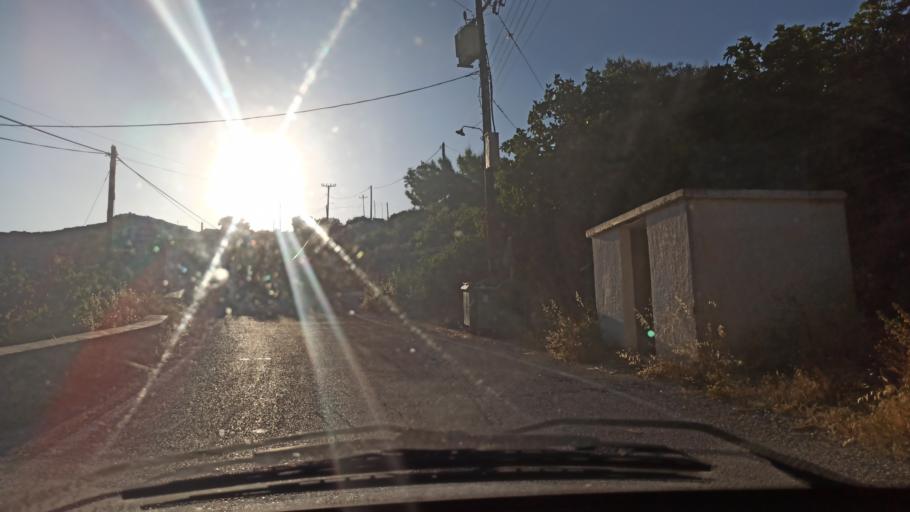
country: GR
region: South Aegean
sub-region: Nomos Kykladon
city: Ano Syros
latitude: 37.4631
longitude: 24.9327
